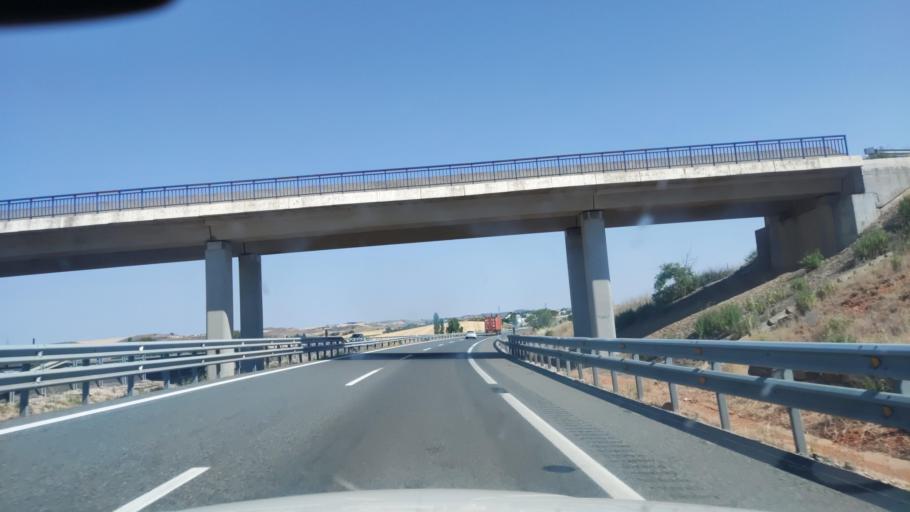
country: ES
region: Castille-La Mancha
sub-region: Provincia de Cuenca
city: Cervera del Llano
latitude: 39.7982
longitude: -2.4379
